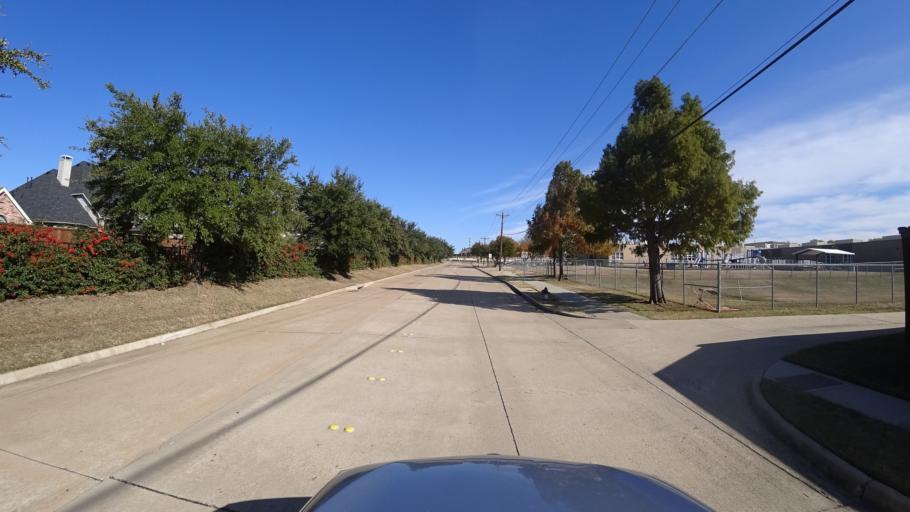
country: US
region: Texas
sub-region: Denton County
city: The Colony
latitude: 33.0270
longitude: -96.9016
